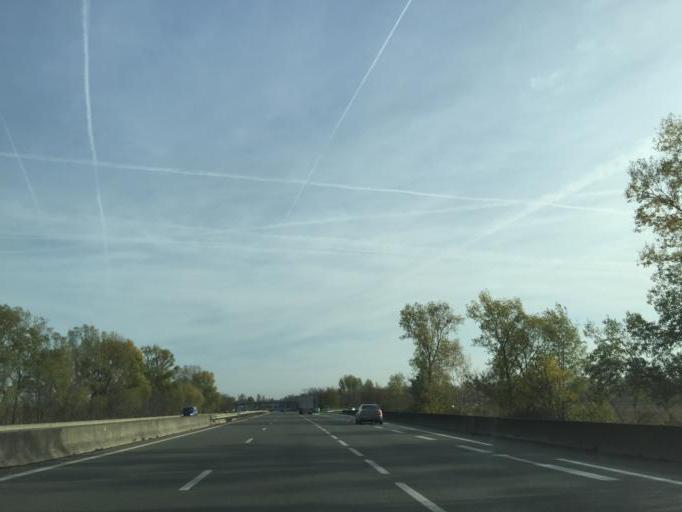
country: FR
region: Rhone-Alpes
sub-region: Departement de l'Ain
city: Saint-Maurice-de-Beynost
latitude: 45.8172
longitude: 4.9808
